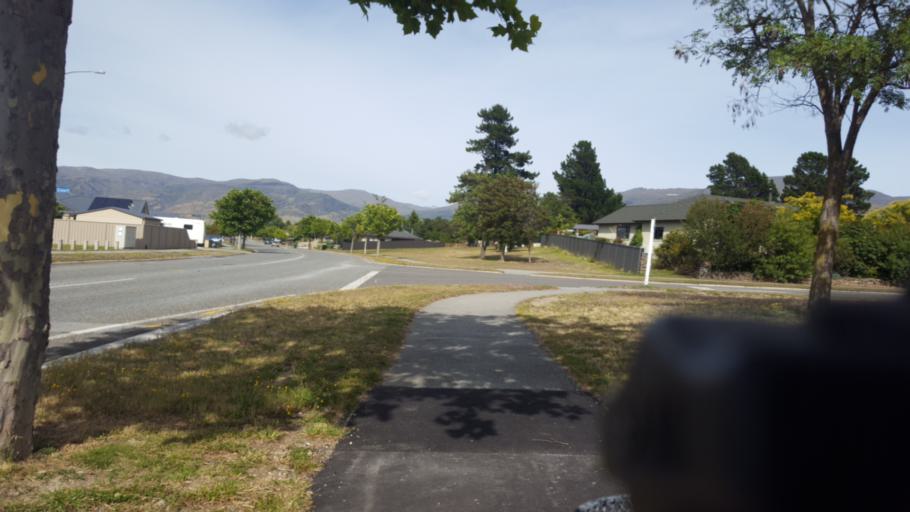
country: NZ
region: Otago
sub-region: Queenstown-Lakes District
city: Wanaka
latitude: -45.0452
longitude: 169.1892
